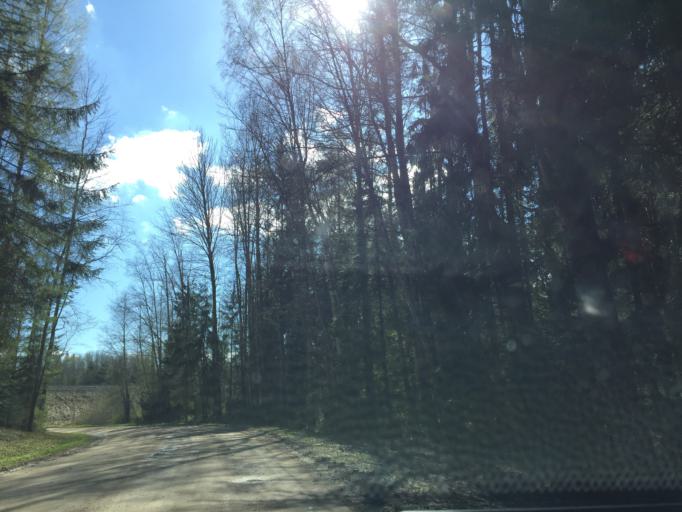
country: EE
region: Valgamaa
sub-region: Valga linn
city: Valga
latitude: 57.8491
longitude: 26.1672
